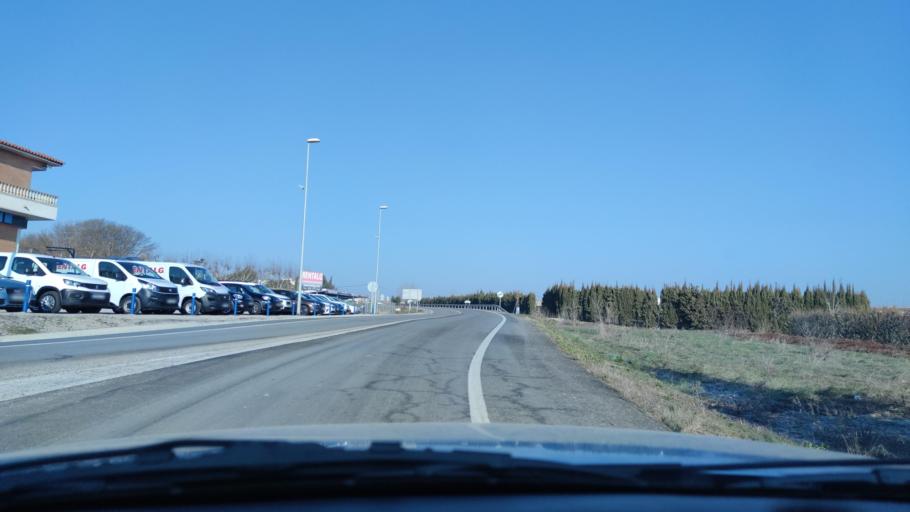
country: ES
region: Catalonia
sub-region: Provincia de Lleida
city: Torrefarrera
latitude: 41.6954
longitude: 0.6363
